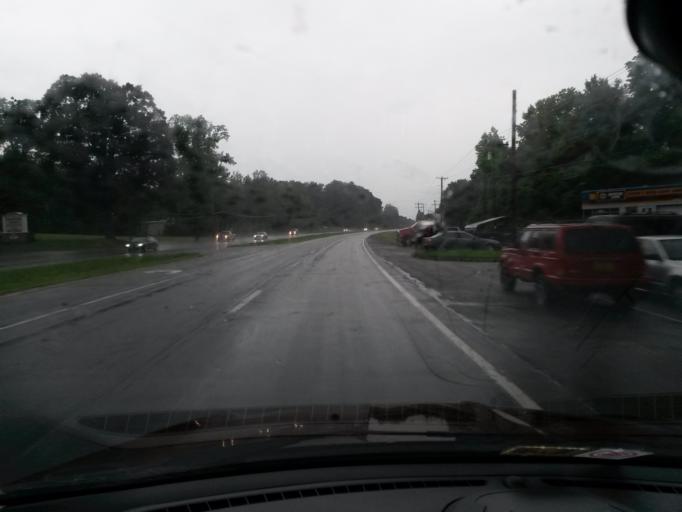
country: US
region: Virginia
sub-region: Chesterfield County
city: Enon
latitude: 37.3257
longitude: -77.3171
